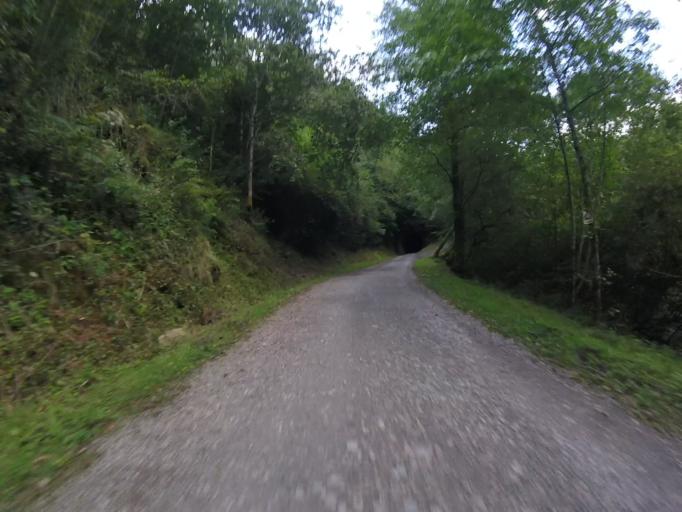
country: ES
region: Basque Country
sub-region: Provincia de Guipuzcoa
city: Berastegui
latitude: 43.1708
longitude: -1.9603
